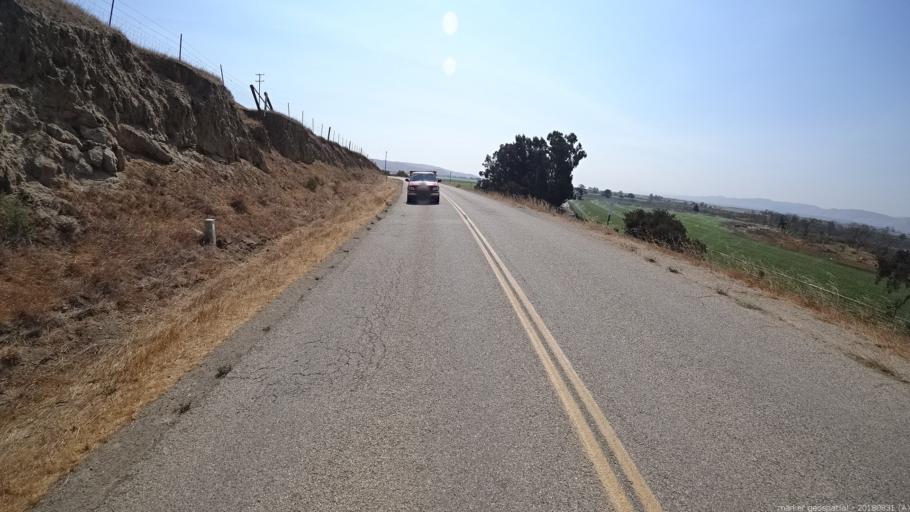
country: US
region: California
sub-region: Monterey County
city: Greenfield
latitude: 36.3630
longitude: -121.2321
